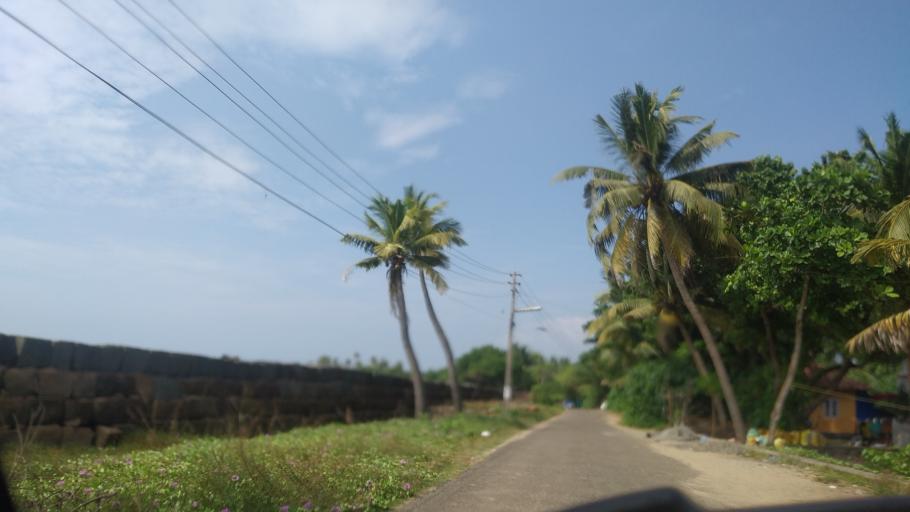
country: IN
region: Kerala
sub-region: Ernakulam
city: Elur
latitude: 10.0496
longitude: 76.2046
